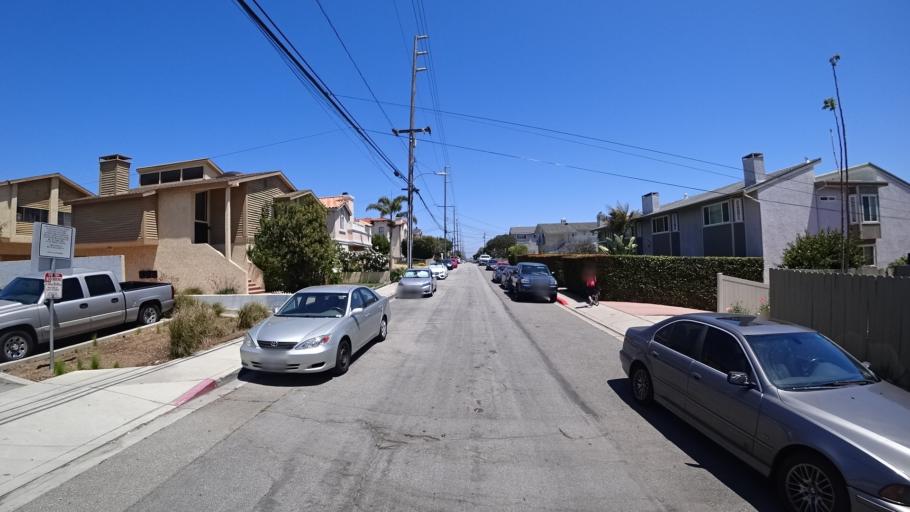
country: US
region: California
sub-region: Los Angeles County
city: Hermosa Beach
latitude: 33.8719
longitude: -118.3766
